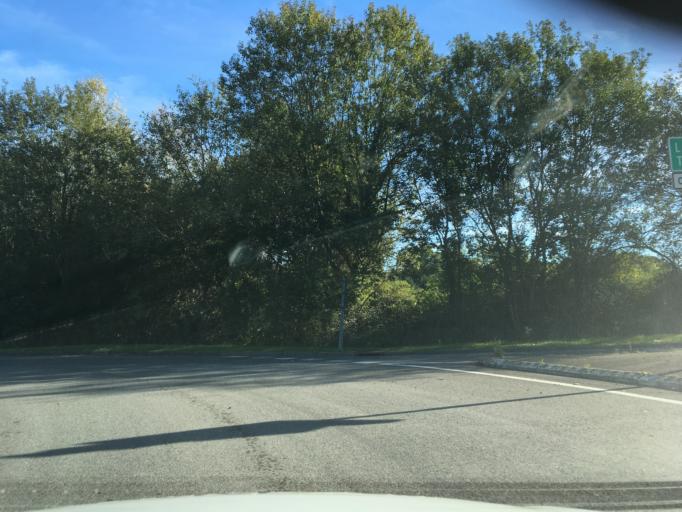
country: FR
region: Aquitaine
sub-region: Departement des Pyrenees-Atlantiques
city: Buros
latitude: 43.3159
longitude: -0.3039
